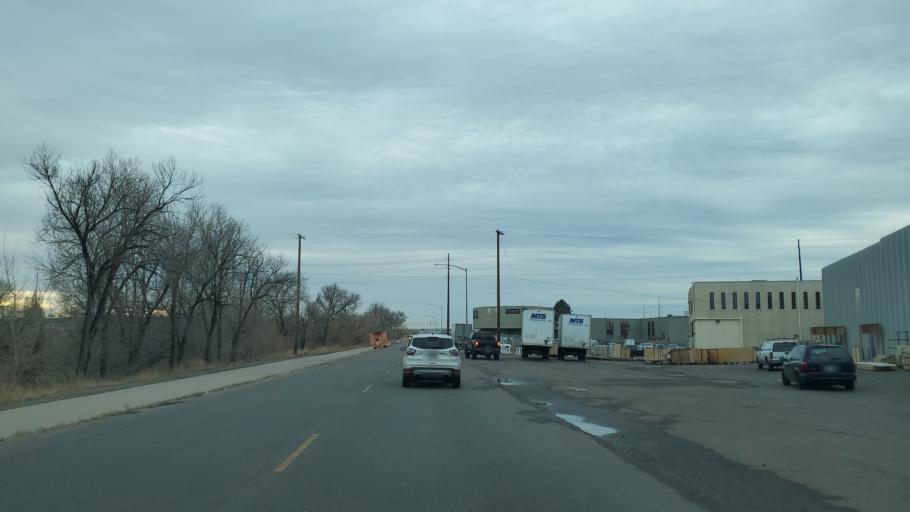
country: US
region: Colorado
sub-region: Denver County
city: Denver
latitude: 39.7105
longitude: -105.0003
